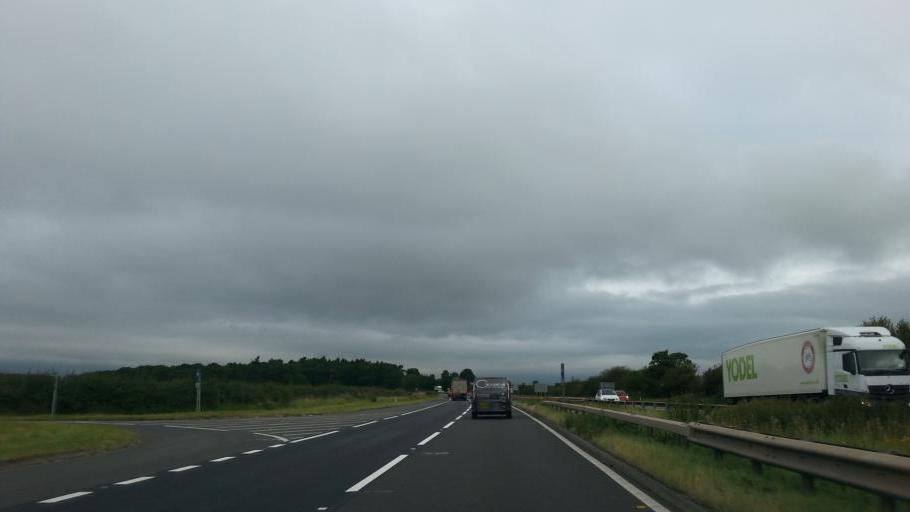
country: GB
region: England
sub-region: Nottinghamshire
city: Babworth
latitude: 53.3445
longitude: -1.0308
